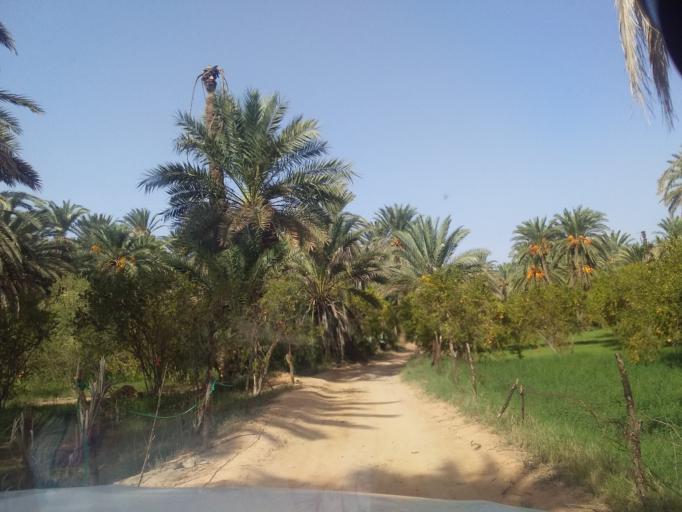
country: TN
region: Qabis
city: Gabes
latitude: 33.6249
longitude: 10.2896
